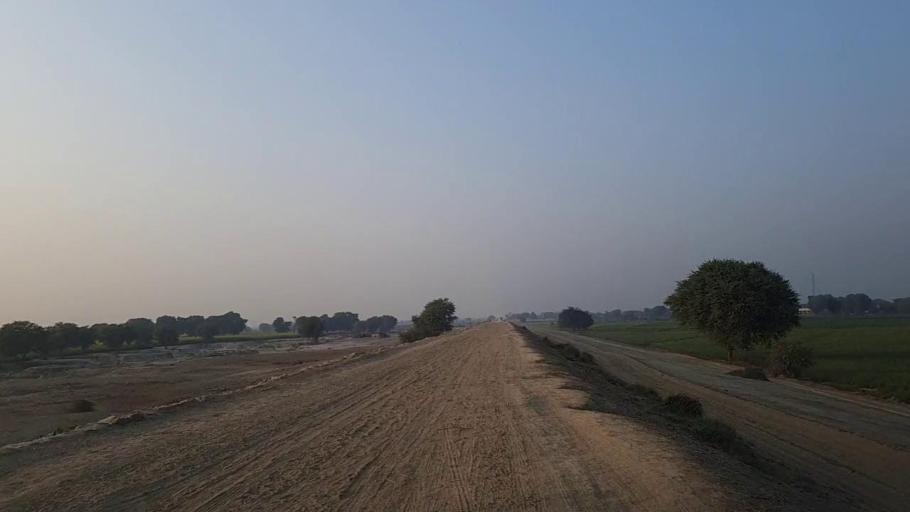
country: PK
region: Sindh
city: Sann
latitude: 26.1858
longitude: 68.0931
